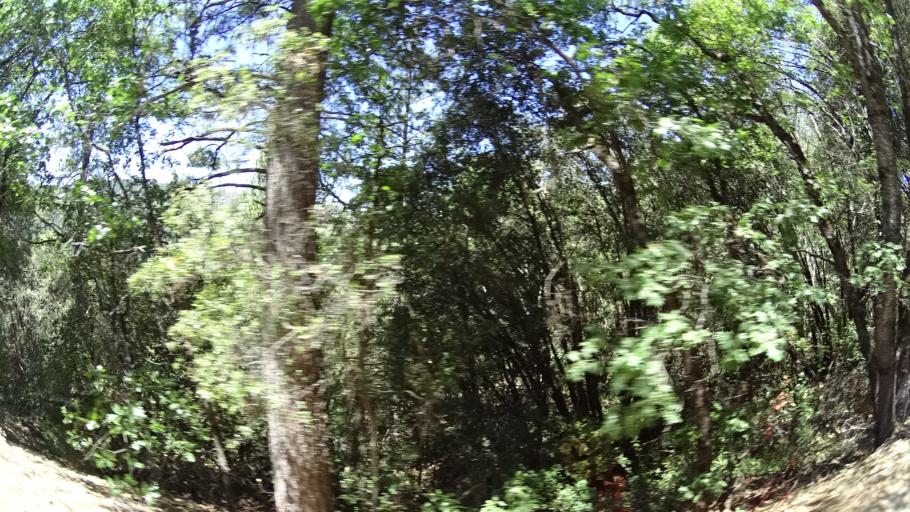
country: US
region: California
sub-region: Amador County
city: Pioneer
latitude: 38.3739
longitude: -120.5595
